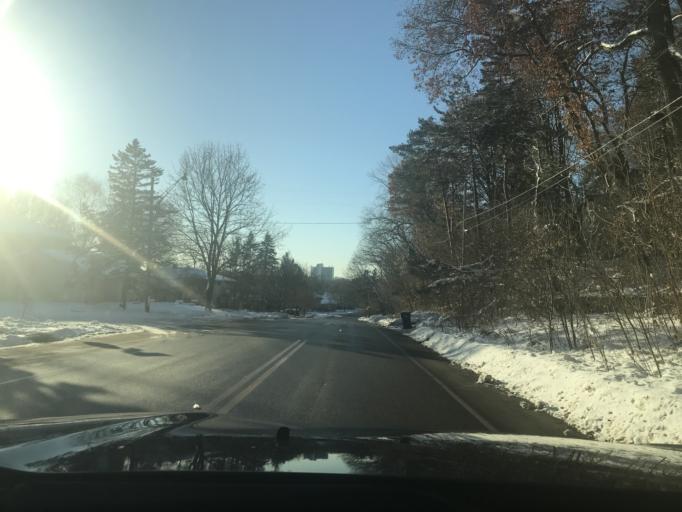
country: US
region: Minnesota
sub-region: Dakota County
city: Mendota Heights
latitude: 44.9217
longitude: -93.1467
